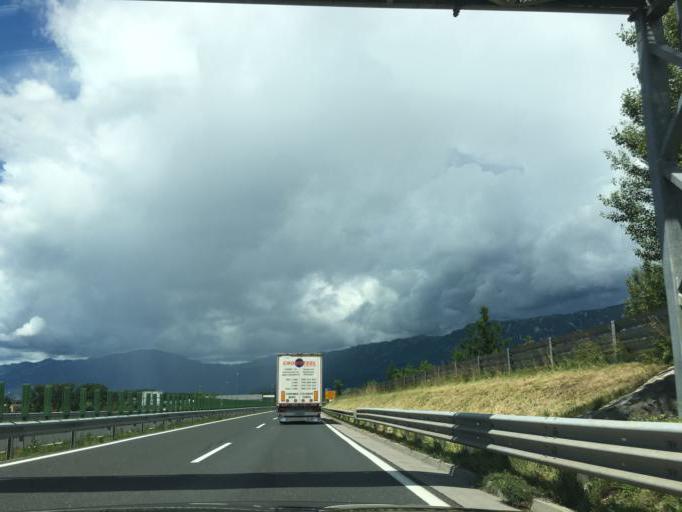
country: SI
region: Vipava
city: Vipava
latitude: 45.8324
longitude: 13.9561
